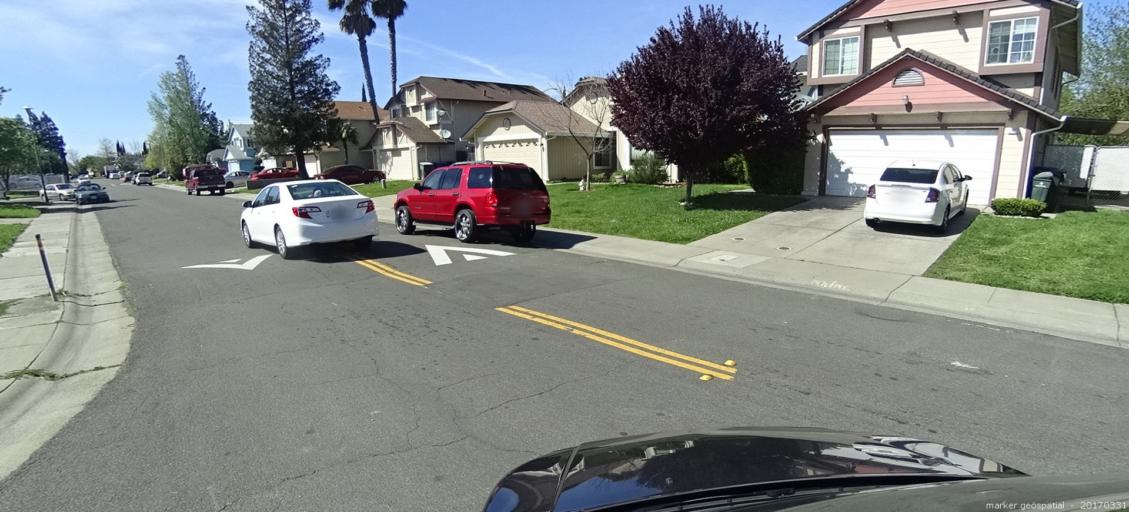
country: US
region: California
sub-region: Sacramento County
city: Laguna
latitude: 38.4589
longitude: -121.4333
